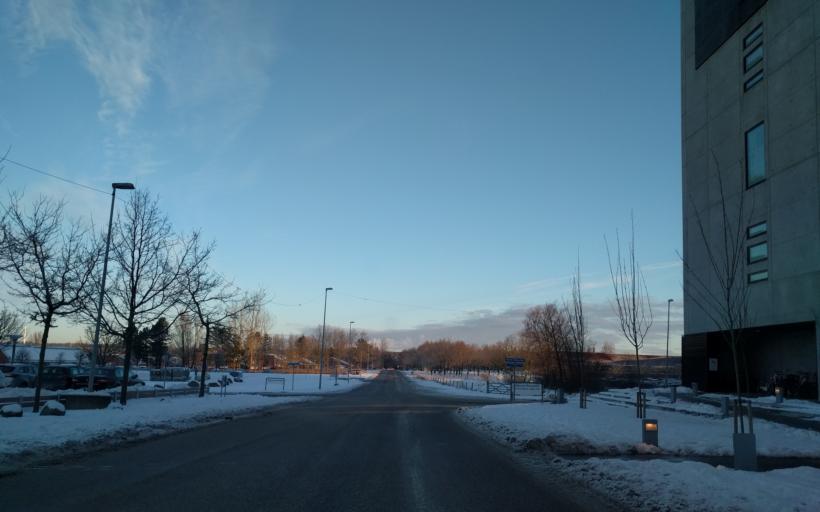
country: DK
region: North Denmark
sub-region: Alborg Kommune
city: Gistrup
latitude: 57.0145
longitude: 9.9844
